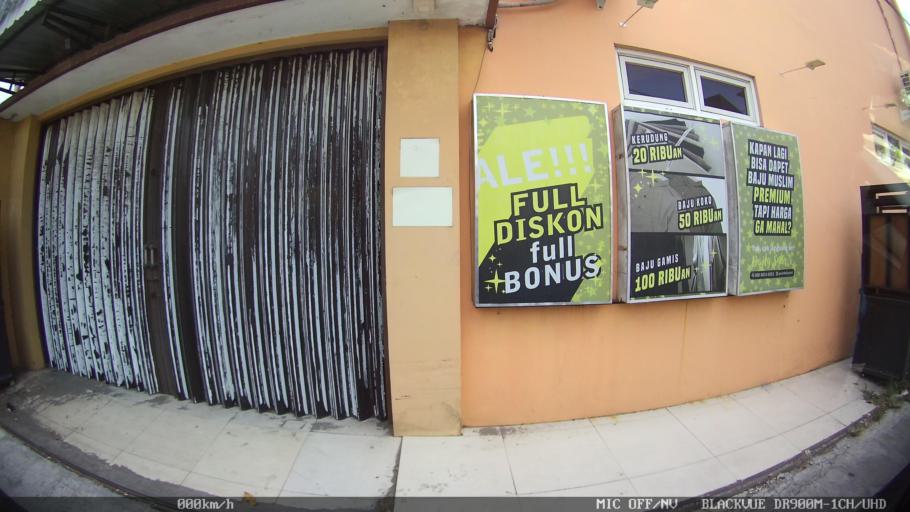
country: ID
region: Daerah Istimewa Yogyakarta
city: Gamping Lor
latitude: -7.8068
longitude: 110.3407
